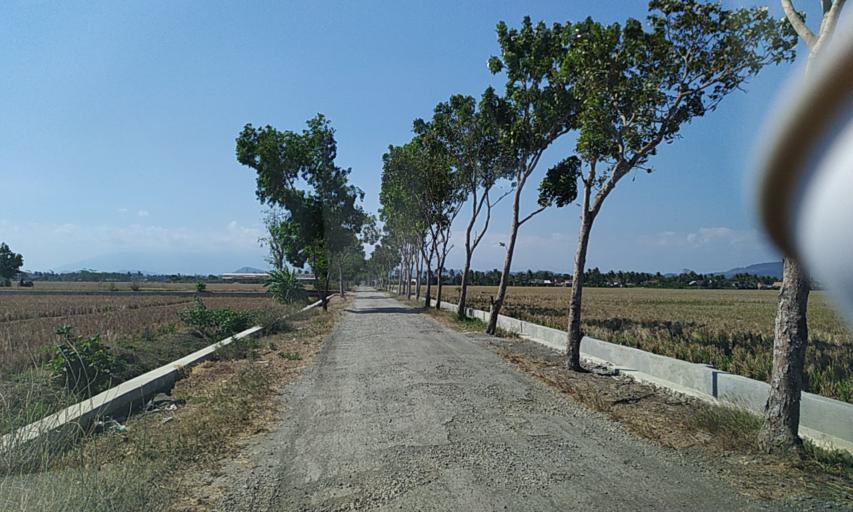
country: ID
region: Central Java
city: Mernek
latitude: -7.6015
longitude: 109.1711
